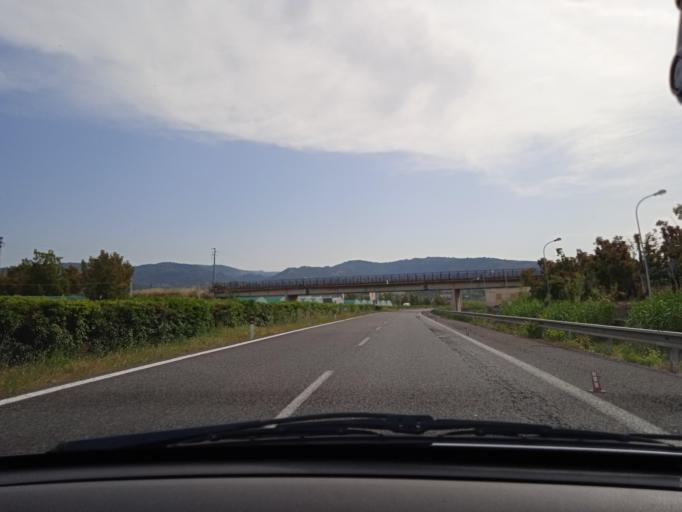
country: IT
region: Sicily
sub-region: Messina
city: Tonnarella
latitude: 38.1177
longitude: 15.1119
